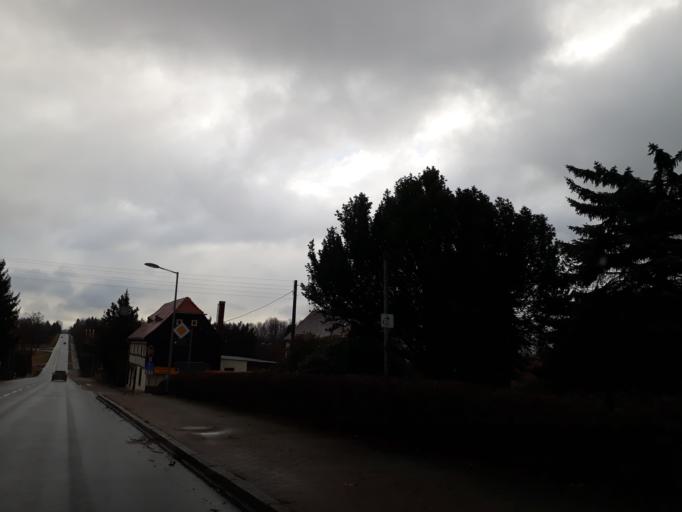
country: DE
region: Saxony
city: Herrnhut
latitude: 51.0287
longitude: 14.7228
